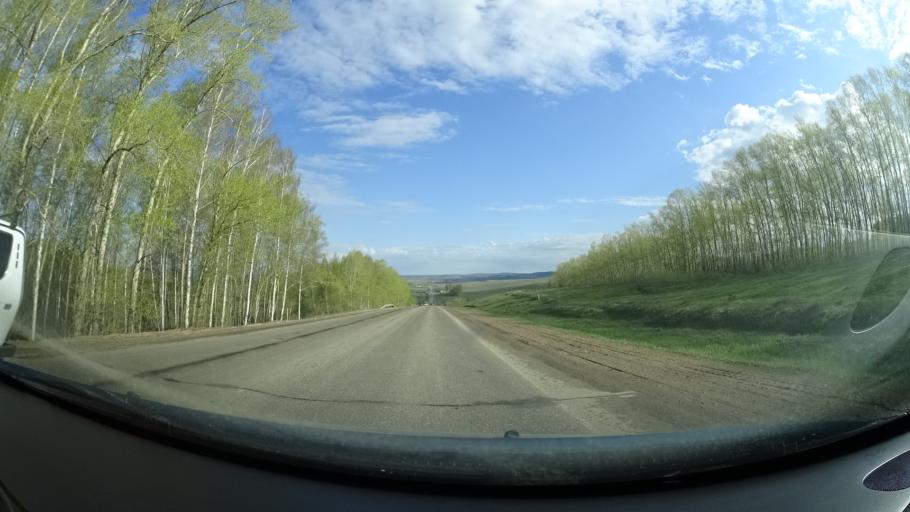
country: RU
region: Bashkortostan
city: Blagoveshchensk
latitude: 55.1592
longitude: 55.8531
